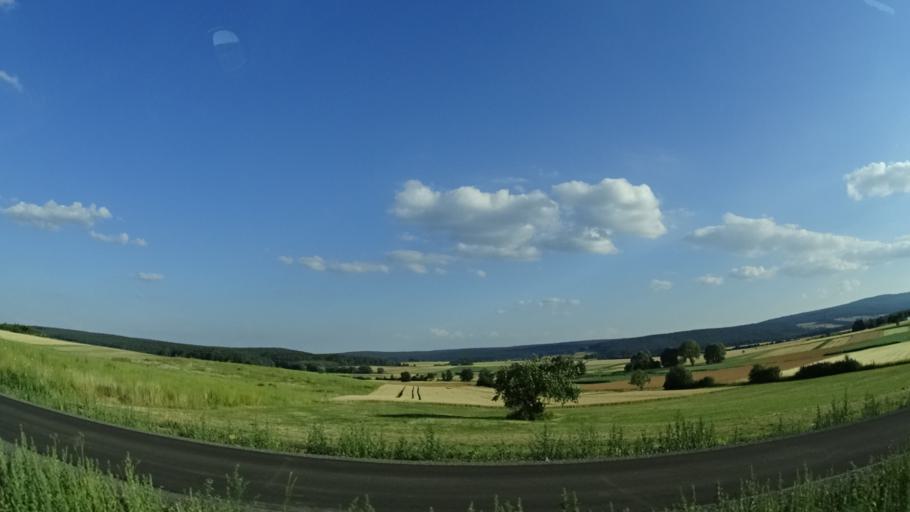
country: DE
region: Bavaria
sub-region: Regierungsbezirk Unterfranken
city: Oberelsbach
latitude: 50.4217
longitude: 10.0857
